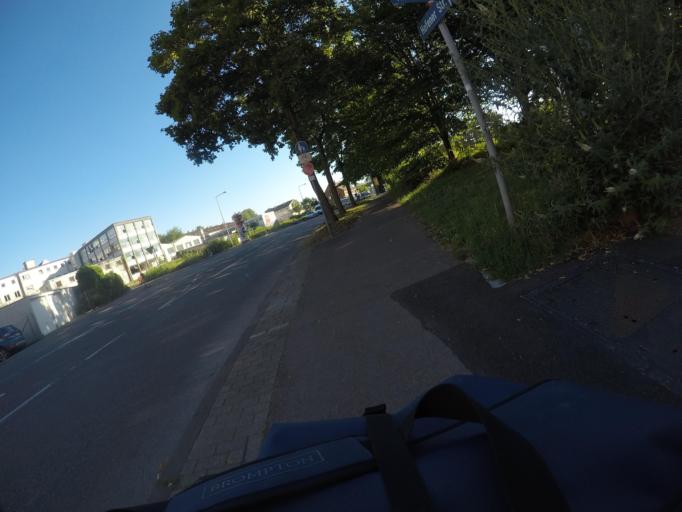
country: DE
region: Baden-Wuerttemberg
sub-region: Regierungsbezirk Stuttgart
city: Stuttgart Muehlhausen
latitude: 48.8167
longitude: 9.2293
